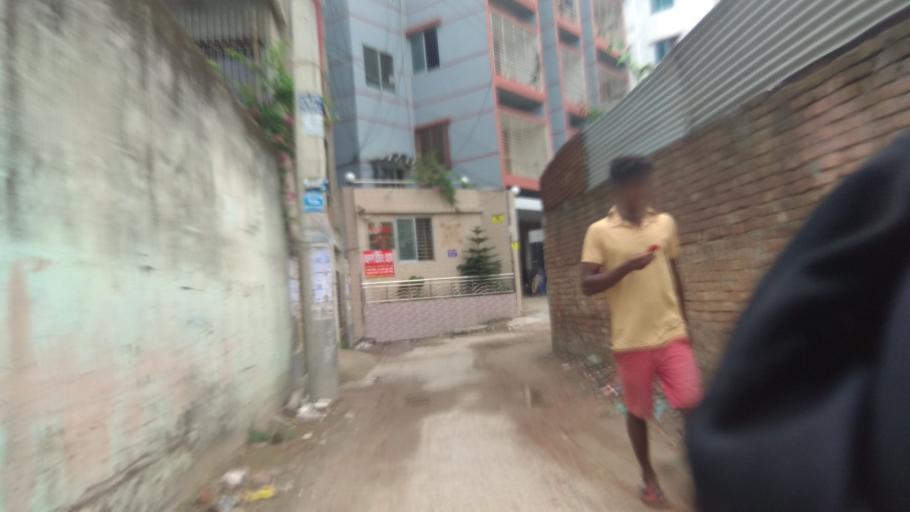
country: BD
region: Dhaka
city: Azimpur
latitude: 23.7968
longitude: 90.3601
